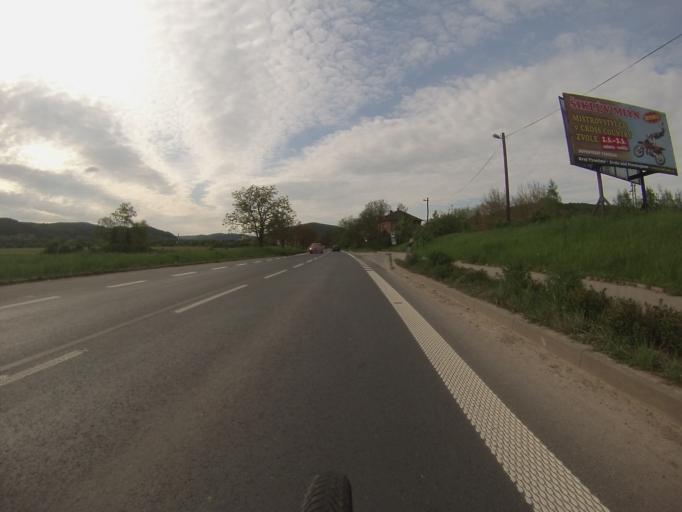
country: CZ
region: South Moravian
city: Tisnov
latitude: 49.3328
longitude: 16.4385
